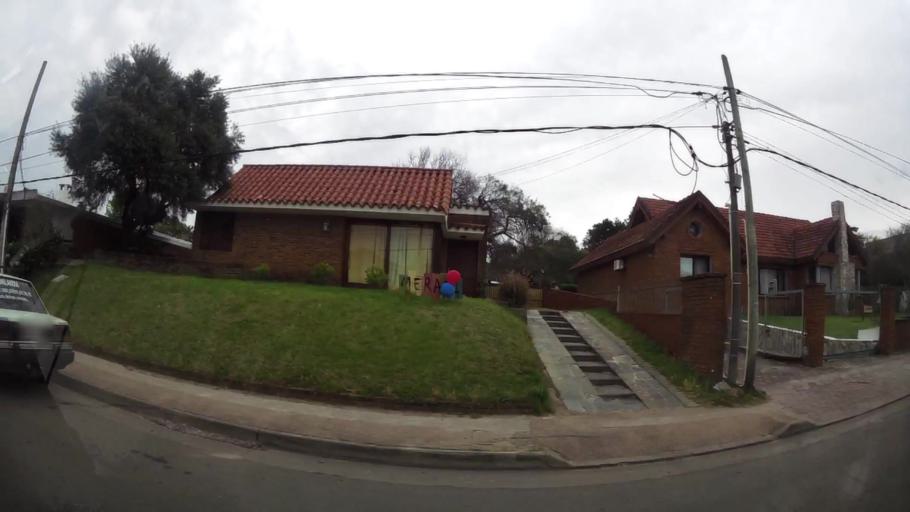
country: UY
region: Maldonado
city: Maldonado
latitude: -34.9160
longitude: -54.9693
